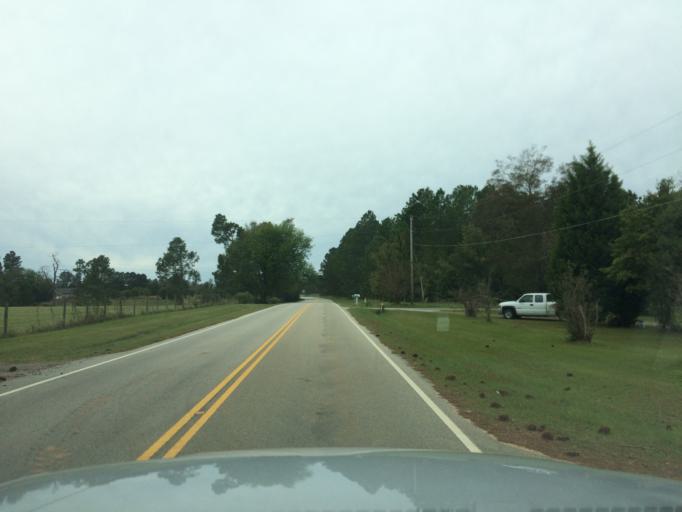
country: US
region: South Carolina
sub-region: Aiken County
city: New Ellenton
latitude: 33.4630
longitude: -81.6824
